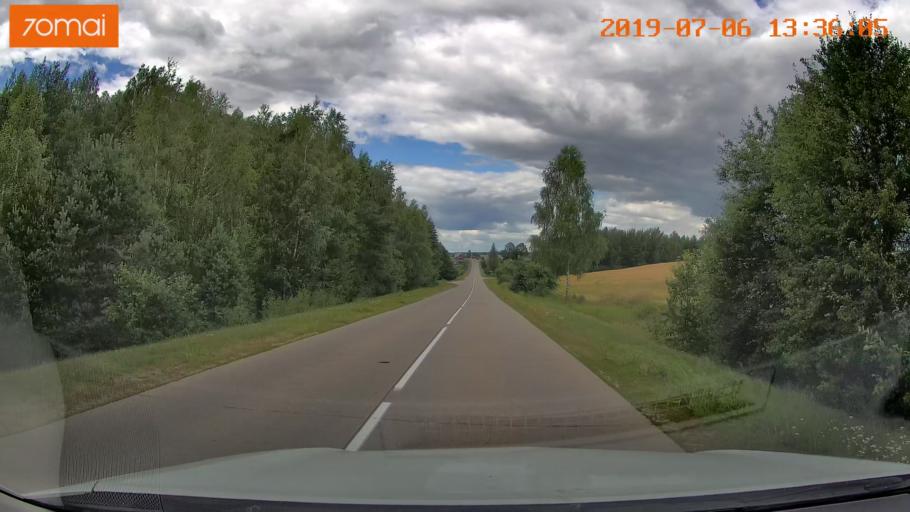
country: BY
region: Minsk
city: Enyerhyetykaw
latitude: 53.6866
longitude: 26.8711
